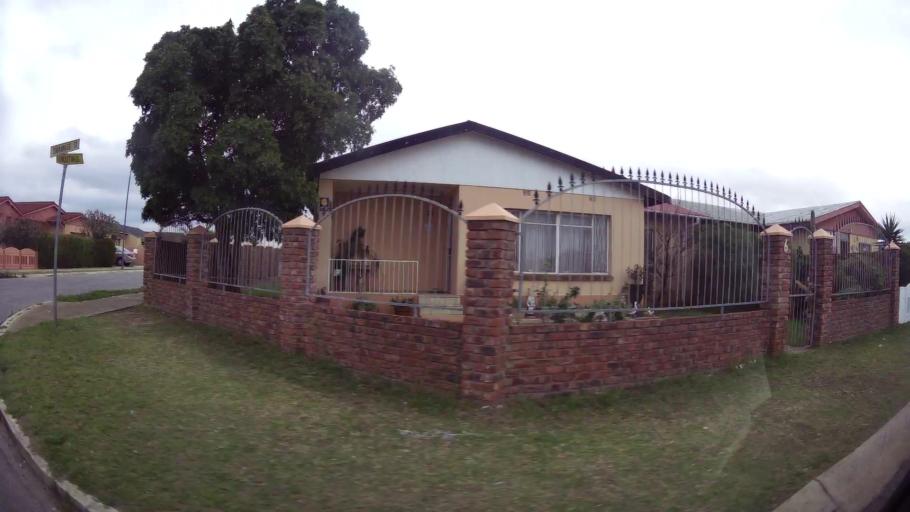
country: ZA
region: Eastern Cape
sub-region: Nelson Mandela Bay Metropolitan Municipality
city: Port Elizabeth
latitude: -33.9032
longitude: 25.5652
